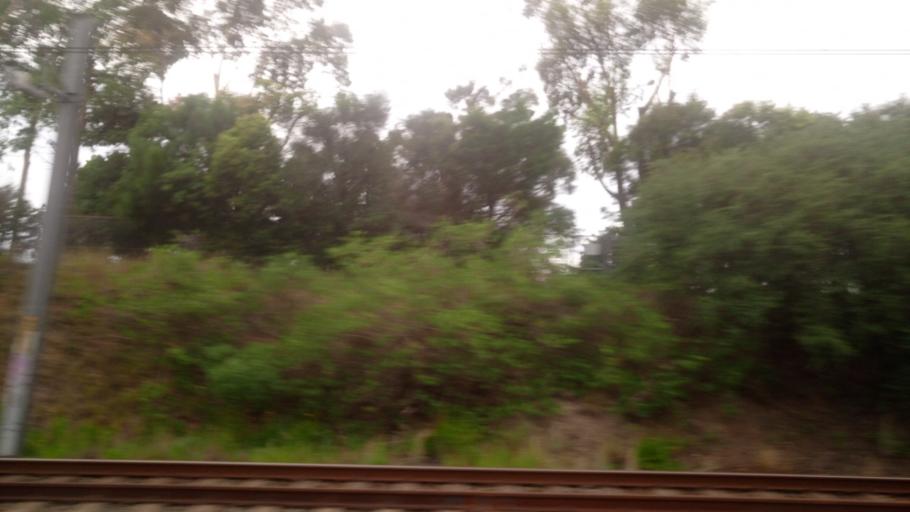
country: AU
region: New South Wales
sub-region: Auburn
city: Lidcombe
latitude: -33.8645
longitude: 151.0511
